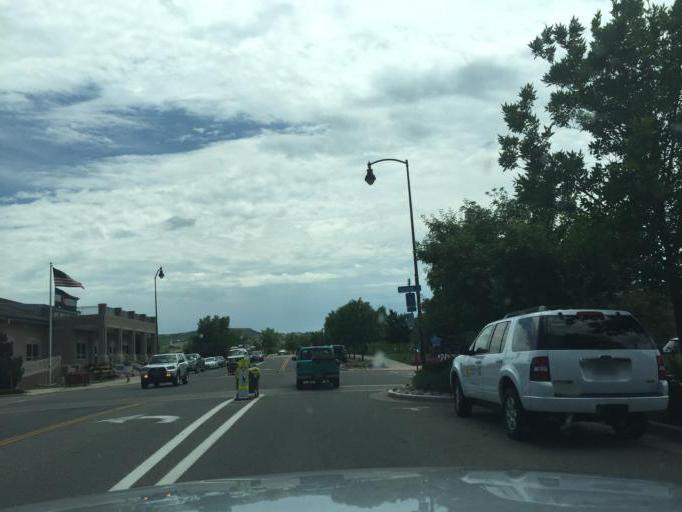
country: US
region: Colorado
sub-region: Douglas County
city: Castle Rock
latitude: 39.3716
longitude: -104.8587
